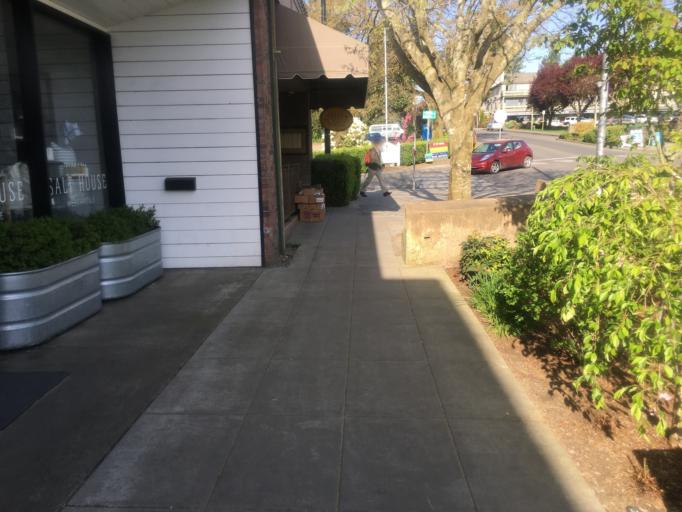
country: US
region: Washington
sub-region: Kitsap County
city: Bainbridge Island
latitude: 47.6247
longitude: -122.5206
